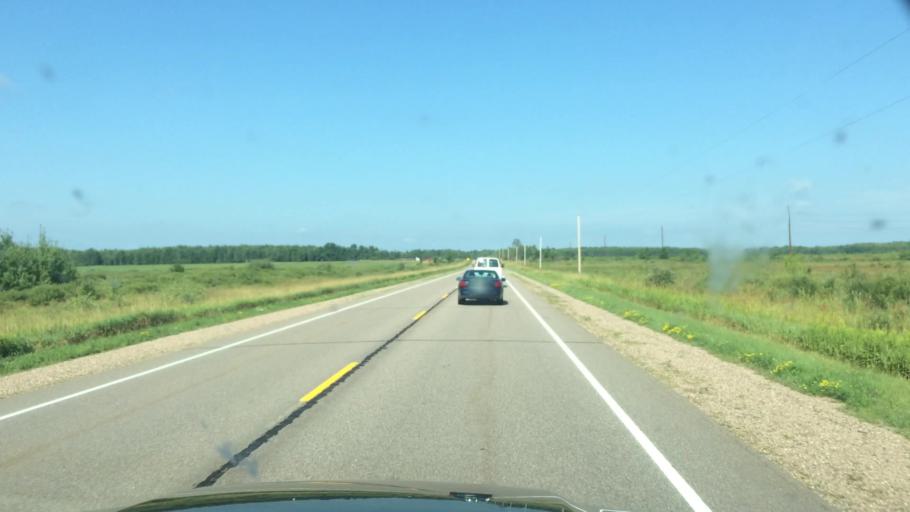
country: US
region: Wisconsin
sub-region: Langlade County
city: Antigo
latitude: 45.1472
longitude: -89.4007
